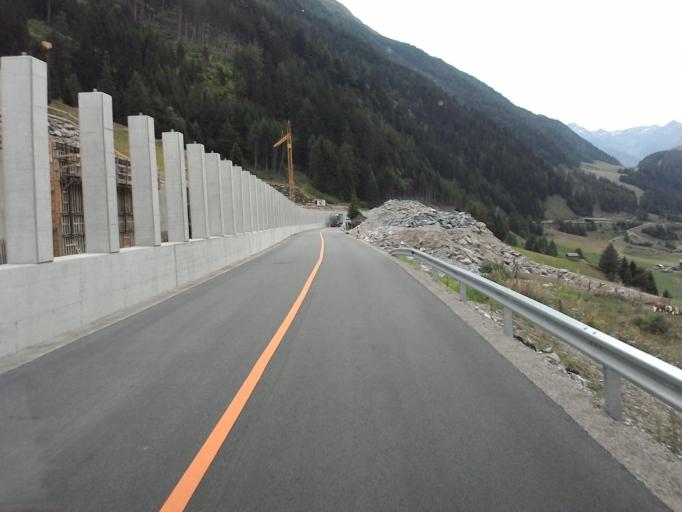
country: AT
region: Tyrol
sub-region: Politischer Bezirk Lienz
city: Matrei in Osttirol
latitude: 47.0740
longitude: 12.5317
